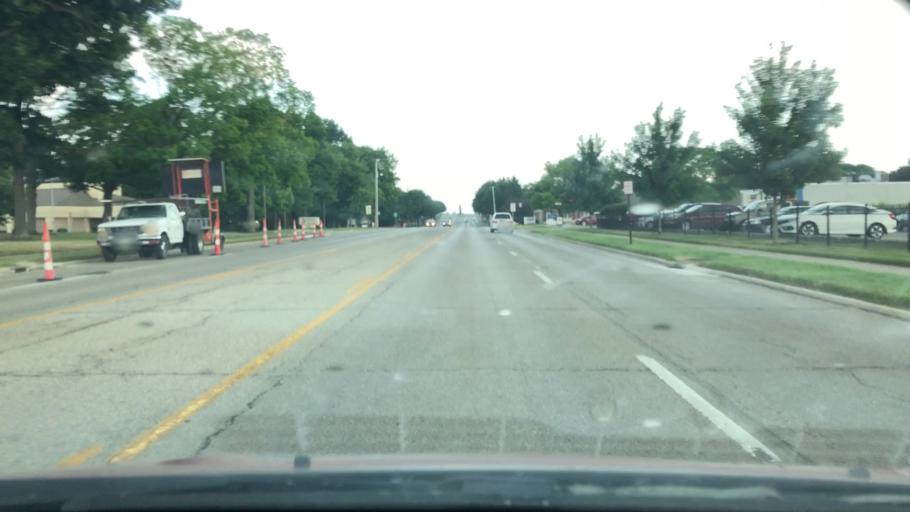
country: US
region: Ohio
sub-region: Montgomery County
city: Centerville
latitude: 39.6592
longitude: -84.1270
